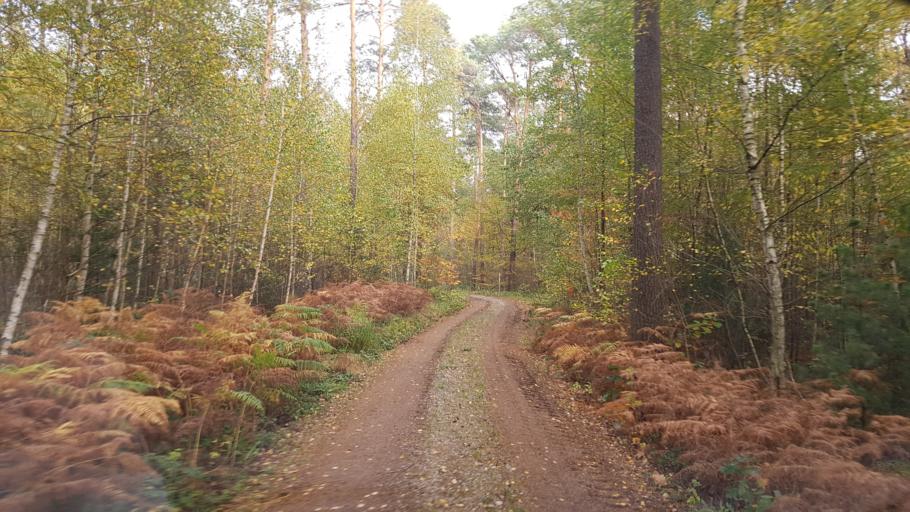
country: DE
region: Brandenburg
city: Doberlug-Kirchhain
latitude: 51.6257
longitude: 13.5237
